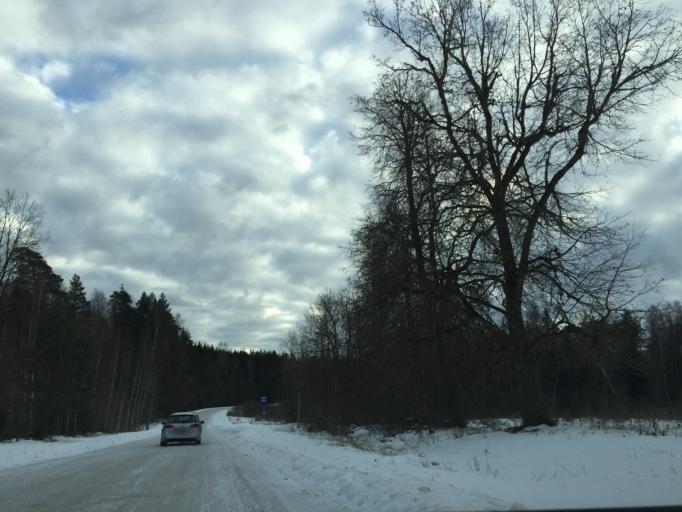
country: LV
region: Lielvarde
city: Lielvarde
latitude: 56.6245
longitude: 24.7721
